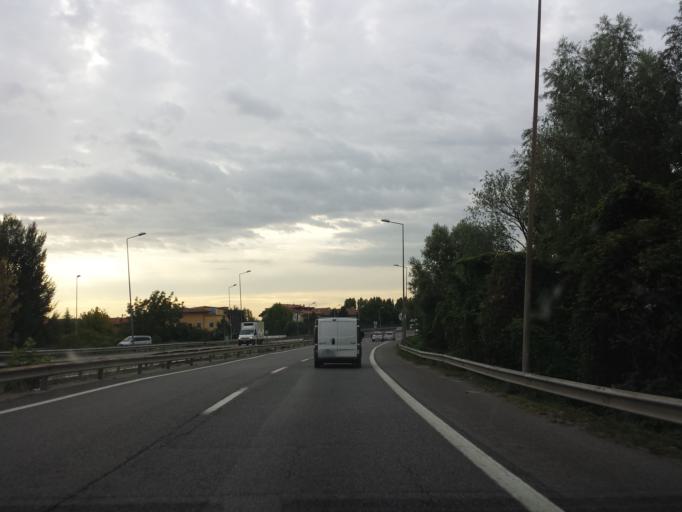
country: IT
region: Veneto
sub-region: Provincia di Padova
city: Mandriola-Sant'Agostino
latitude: 45.3730
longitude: 11.8524
